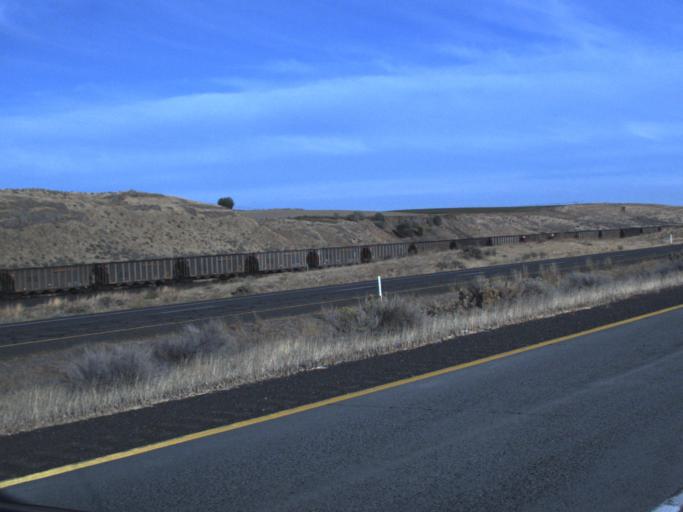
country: US
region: Washington
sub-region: Franklin County
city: Basin City
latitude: 46.4926
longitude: -119.0137
